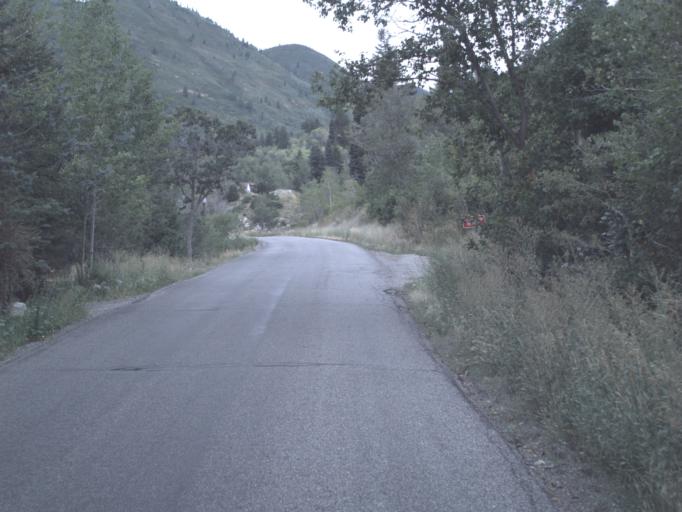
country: US
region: Utah
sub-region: Utah County
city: Lindon
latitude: 40.4030
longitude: -111.5969
